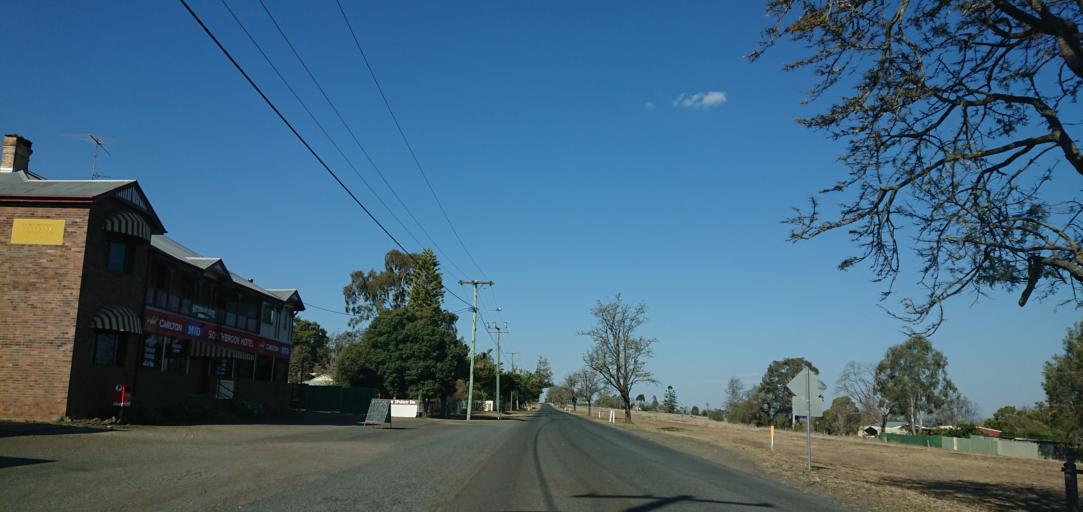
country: AU
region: Queensland
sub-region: Toowoomba
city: Westbrook
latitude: -27.6785
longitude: 151.7140
